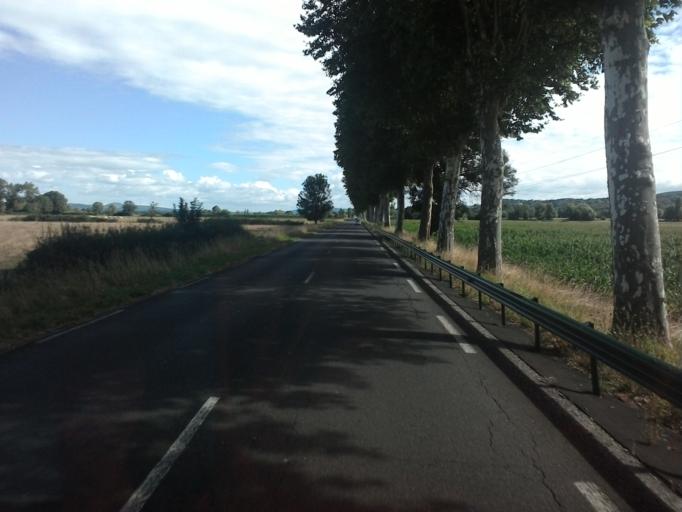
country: FR
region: Rhone-Alpes
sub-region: Departement de l'Ain
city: Ambronay
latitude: 45.9880
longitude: 5.3505
